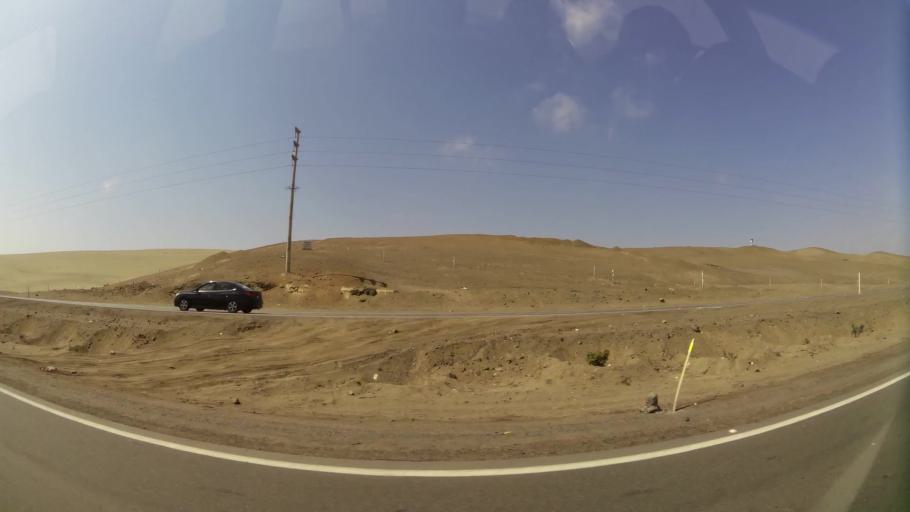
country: PE
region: Lima
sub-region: Provincia de Canete
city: Asia
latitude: -12.8717
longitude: -76.5113
